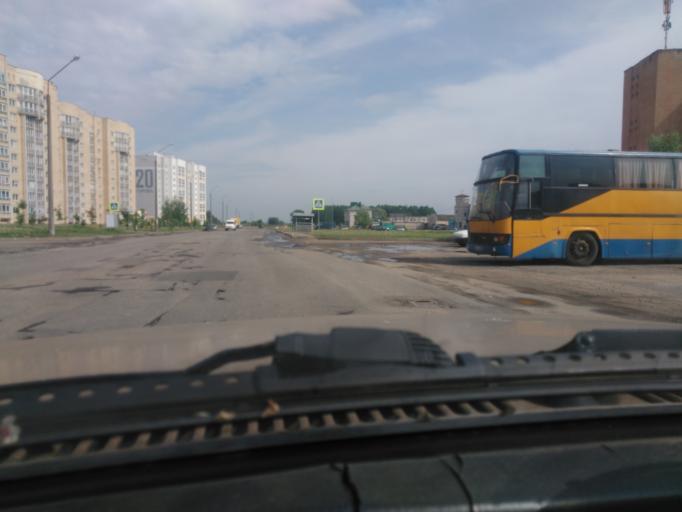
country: BY
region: Mogilev
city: Mahilyow
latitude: 53.9451
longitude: 30.3632
